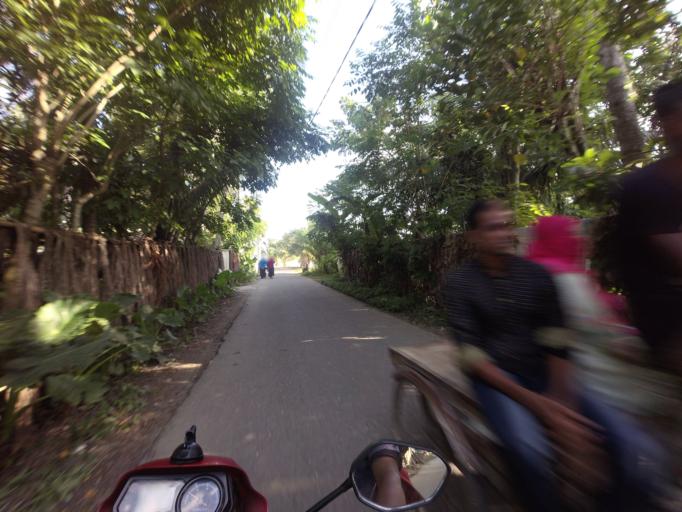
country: BD
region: Khulna
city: Khulna
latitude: 22.9117
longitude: 89.5198
